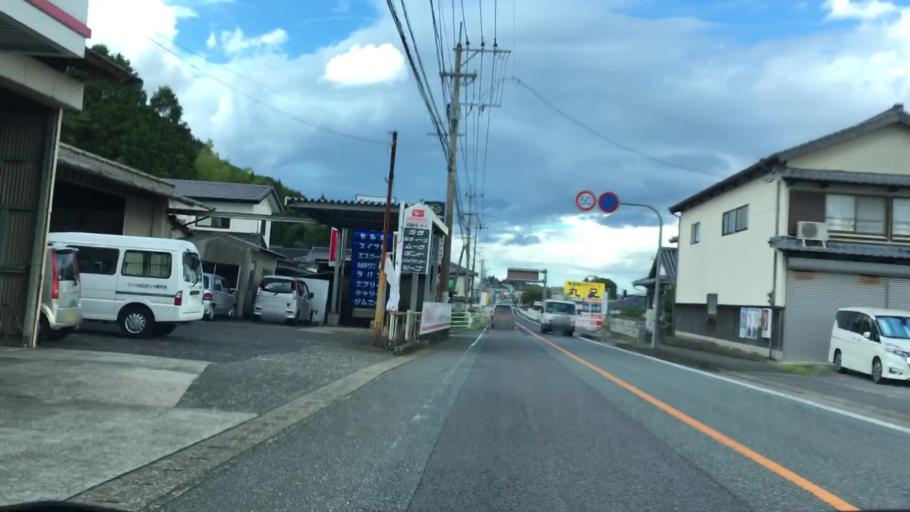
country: JP
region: Saga Prefecture
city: Imaricho-ko
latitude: 33.1983
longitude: 129.8505
